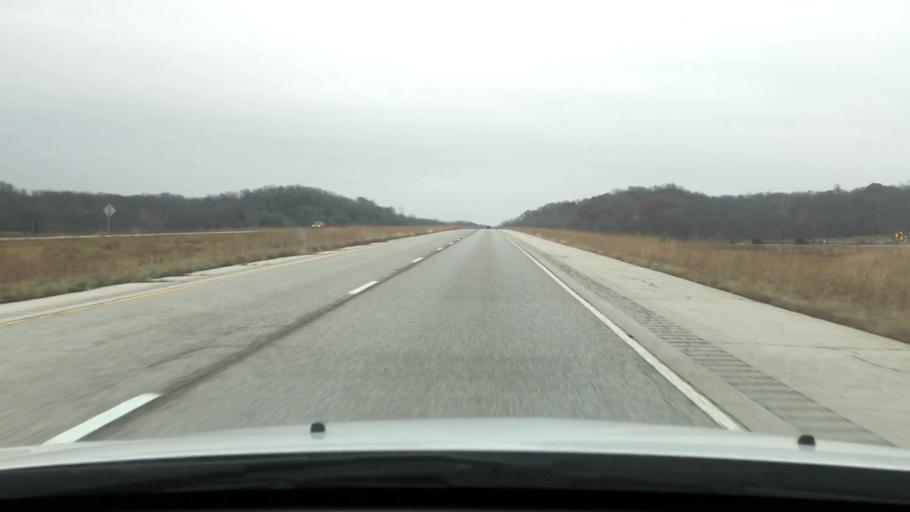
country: US
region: Illinois
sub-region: Scott County
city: Winchester
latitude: 39.6850
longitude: -90.5753
